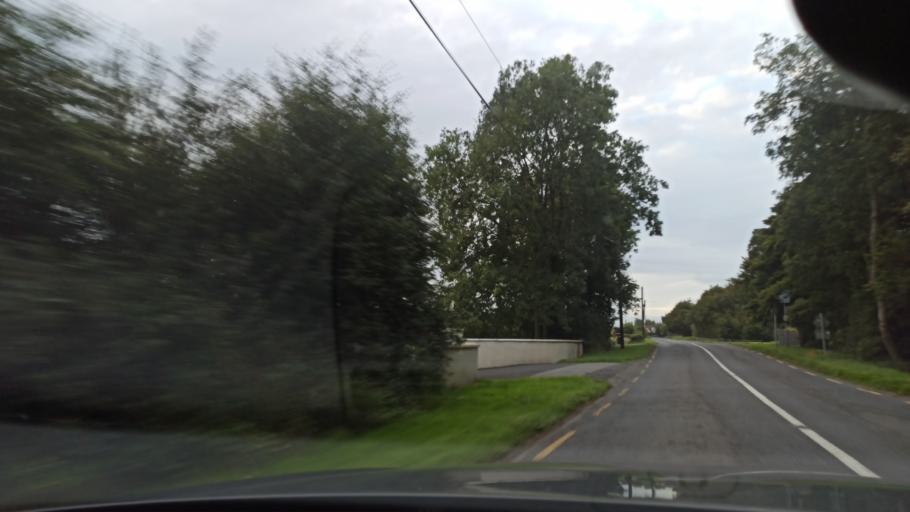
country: IE
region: Munster
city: Cashel
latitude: 52.4920
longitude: -7.8613
